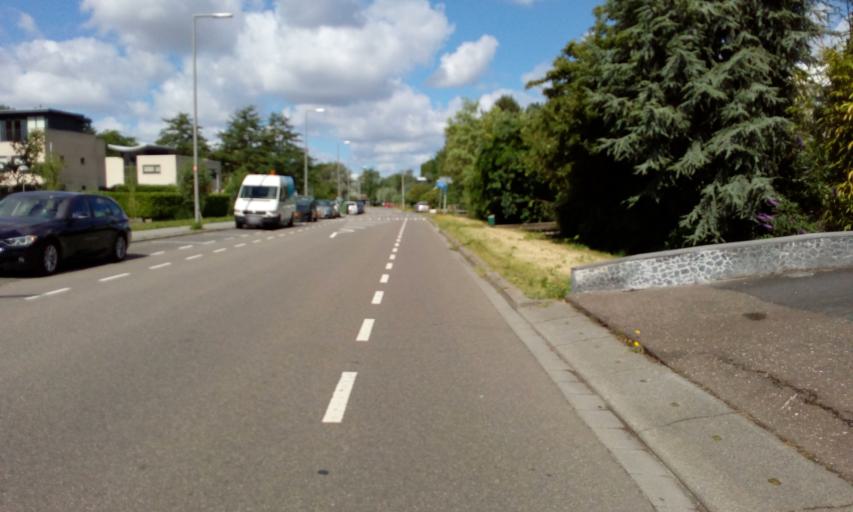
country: NL
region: South Holland
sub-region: Gemeente Rotterdam
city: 's-Gravenland
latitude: 51.9218
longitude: 4.5423
